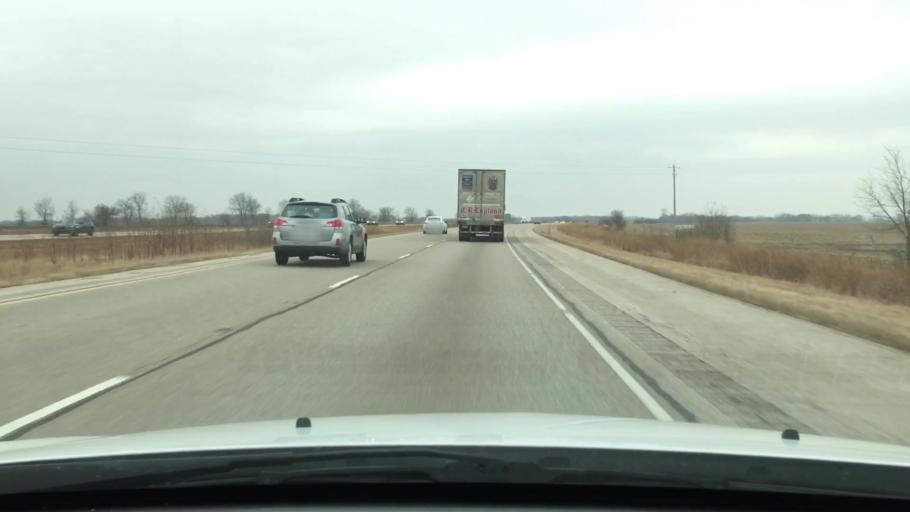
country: US
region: Illinois
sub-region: Logan County
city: Atlanta
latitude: 40.3255
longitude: -89.1547
